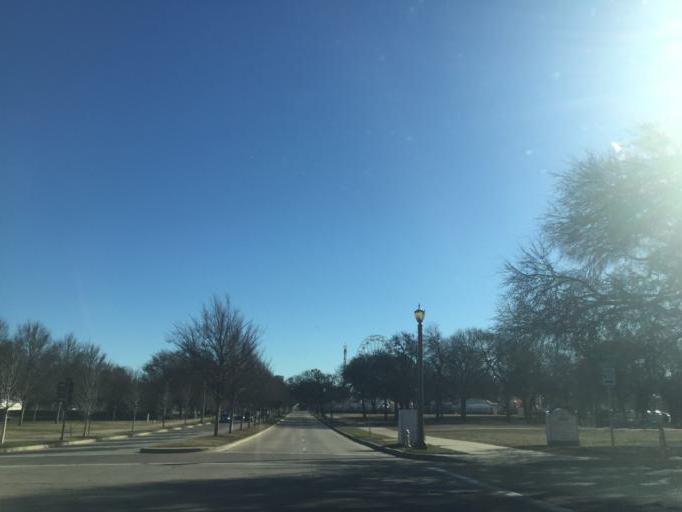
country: US
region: Texas
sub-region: Tarrant County
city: River Oaks
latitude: 32.7474
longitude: -97.3670
